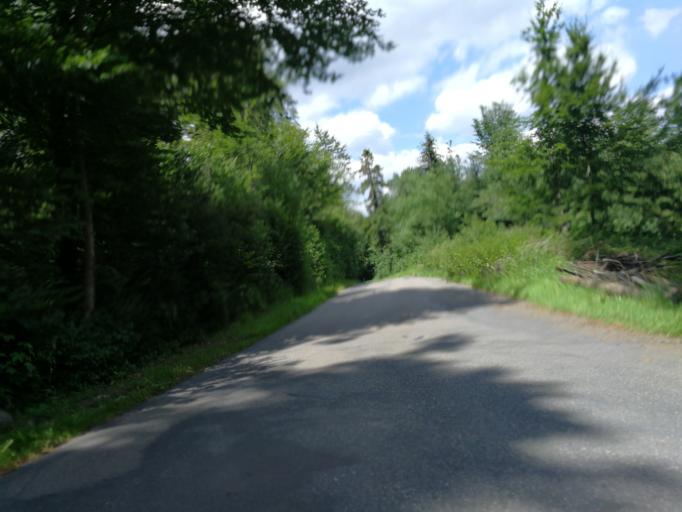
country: CH
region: Zurich
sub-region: Bezirk Hinwil
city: Gruet
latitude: 47.2838
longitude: 8.7876
